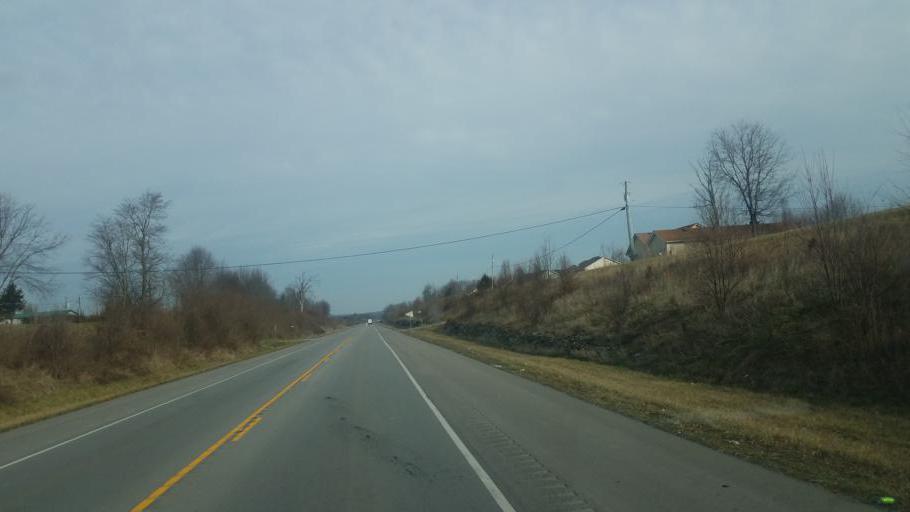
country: US
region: Kentucky
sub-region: Boyle County
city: Junction City
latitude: 37.5218
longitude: -84.8059
